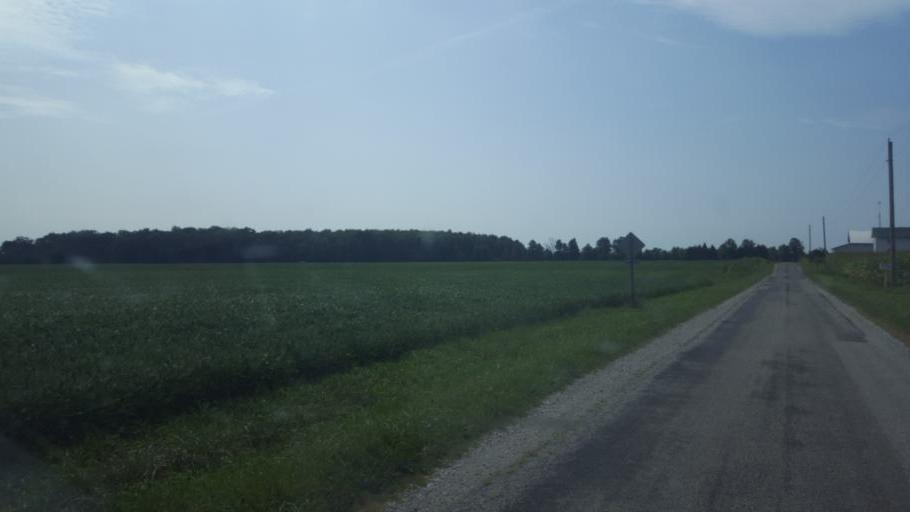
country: US
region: Ohio
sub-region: Delaware County
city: Ashley
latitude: 40.4881
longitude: -83.0247
